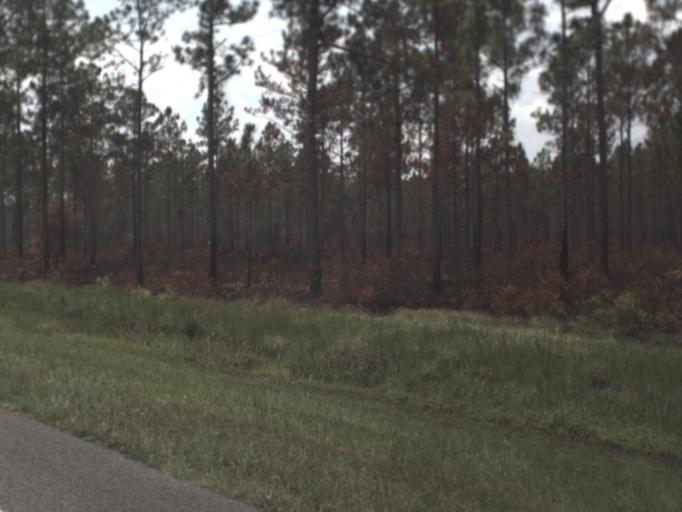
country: US
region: Florida
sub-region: Putnam County
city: Palatka
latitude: 29.5112
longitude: -81.7496
